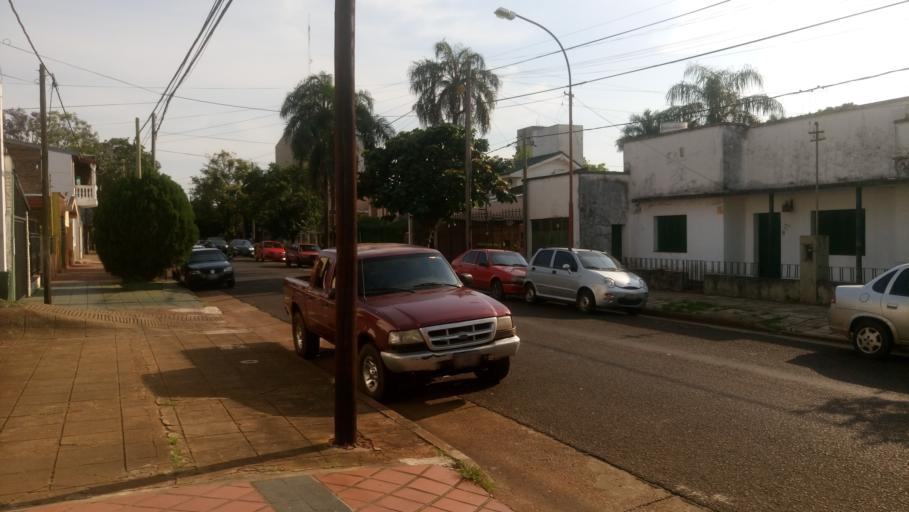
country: AR
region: Misiones
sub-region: Departamento de Capital
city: Posadas
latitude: -27.3761
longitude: -55.8940
